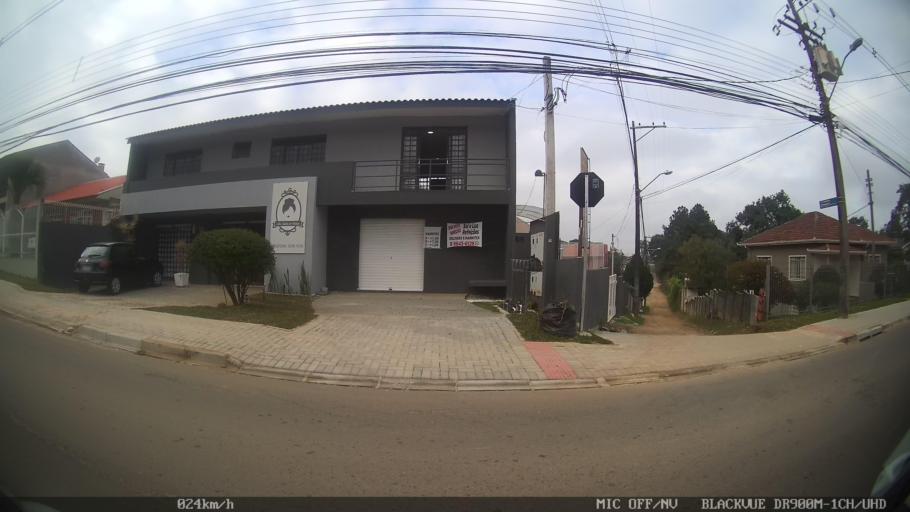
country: BR
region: Parana
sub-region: Curitiba
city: Curitiba
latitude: -25.3982
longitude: -49.3179
